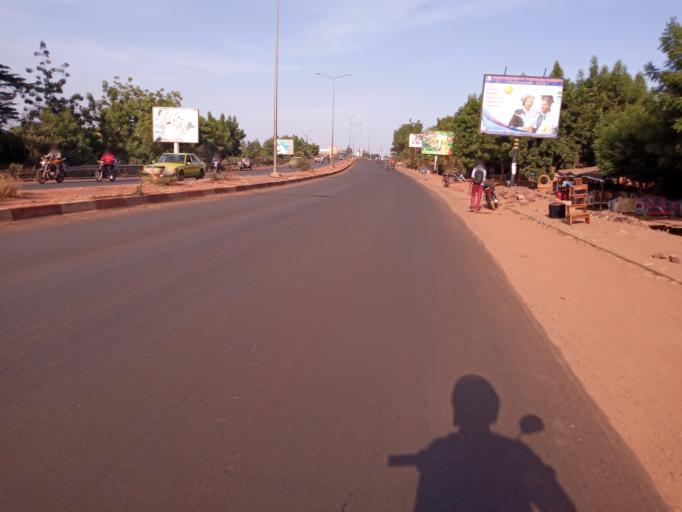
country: ML
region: Bamako
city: Bamako
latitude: 12.6161
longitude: -7.9884
